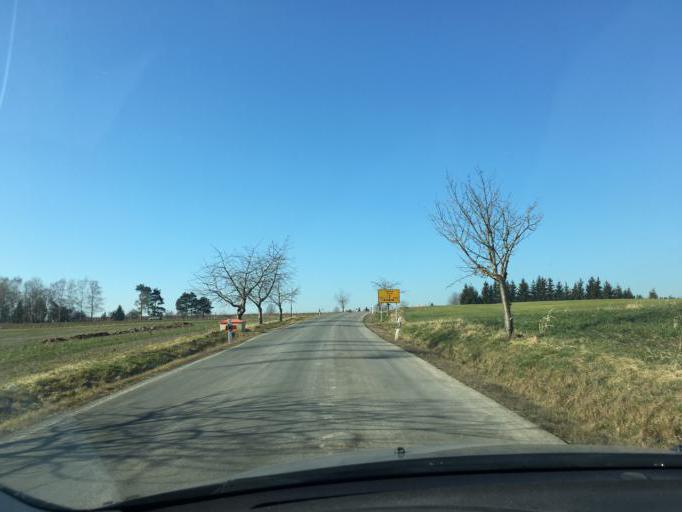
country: DE
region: Saxony
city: Penig
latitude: 50.9711
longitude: 12.6983
